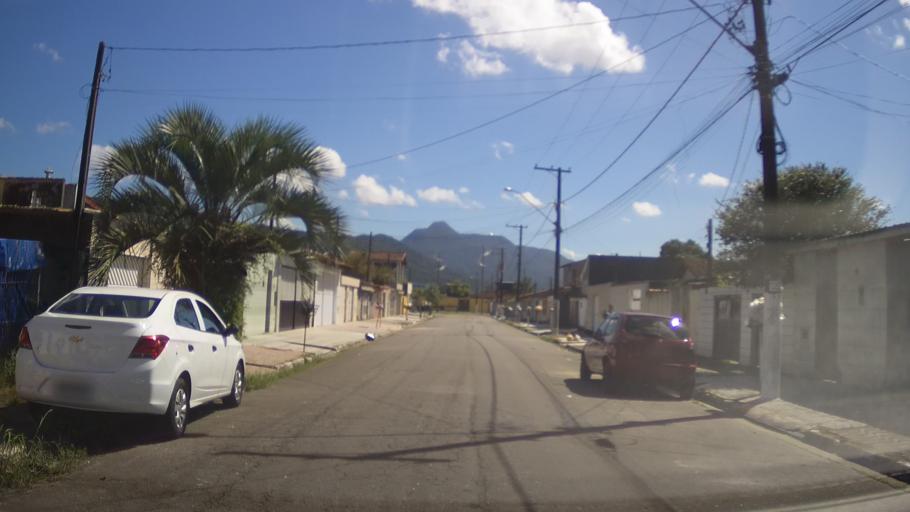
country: BR
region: Sao Paulo
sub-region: Mongagua
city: Mongagua
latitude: -24.0306
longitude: -46.5333
